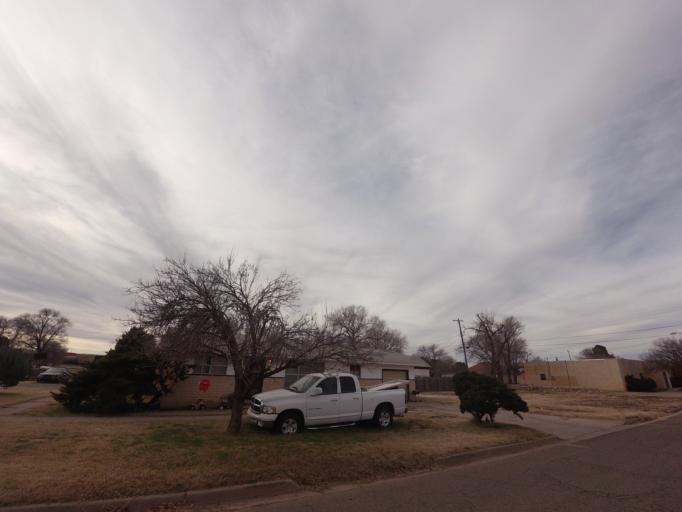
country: US
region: New Mexico
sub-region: Curry County
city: Clovis
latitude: 34.3997
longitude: -103.2144
